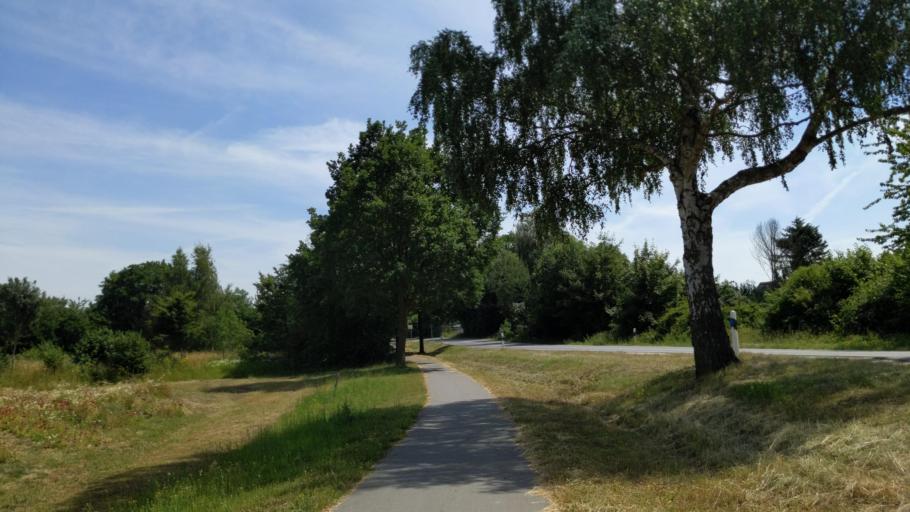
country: DE
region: Schleswig-Holstein
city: Bosdorf
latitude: 54.1488
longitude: 10.5151
